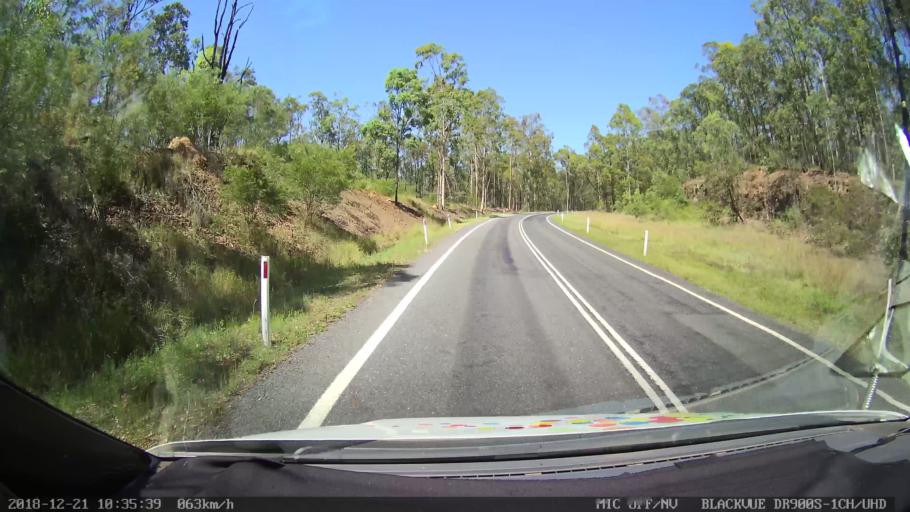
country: AU
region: New South Wales
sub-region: Clarence Valley
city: South Grafton
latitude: -29.6209
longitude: 152.6426
